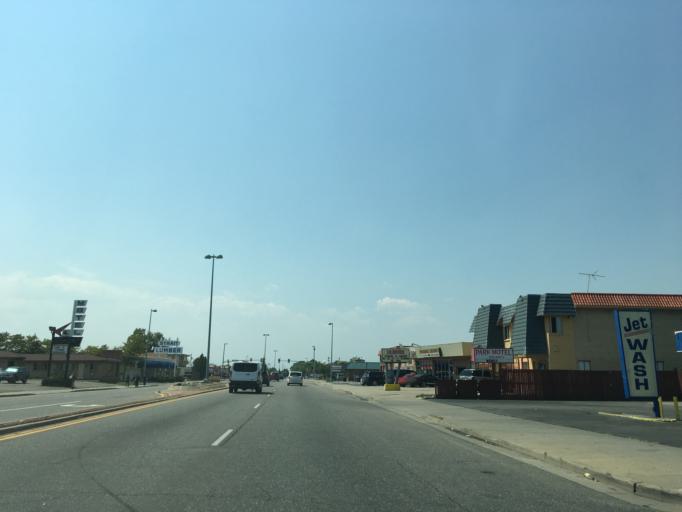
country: US
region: Colorado
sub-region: Adams County
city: Aurora
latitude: 39.7403
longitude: -104.8562
